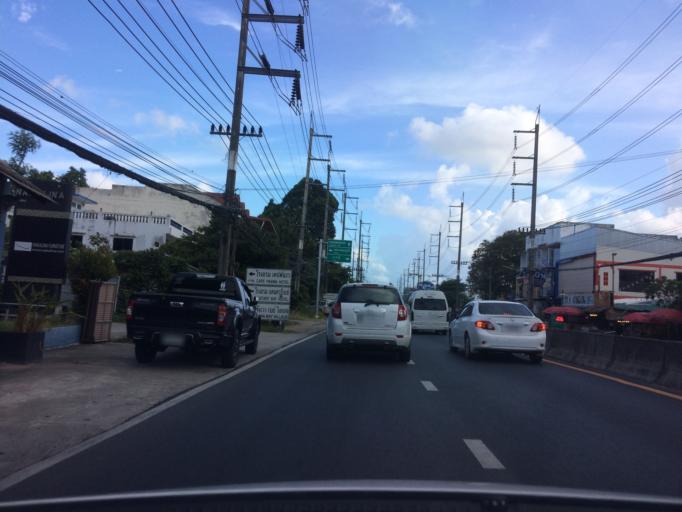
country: TH
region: Phuket
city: Mueang Phuket
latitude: 7.8790
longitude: 98.3636
